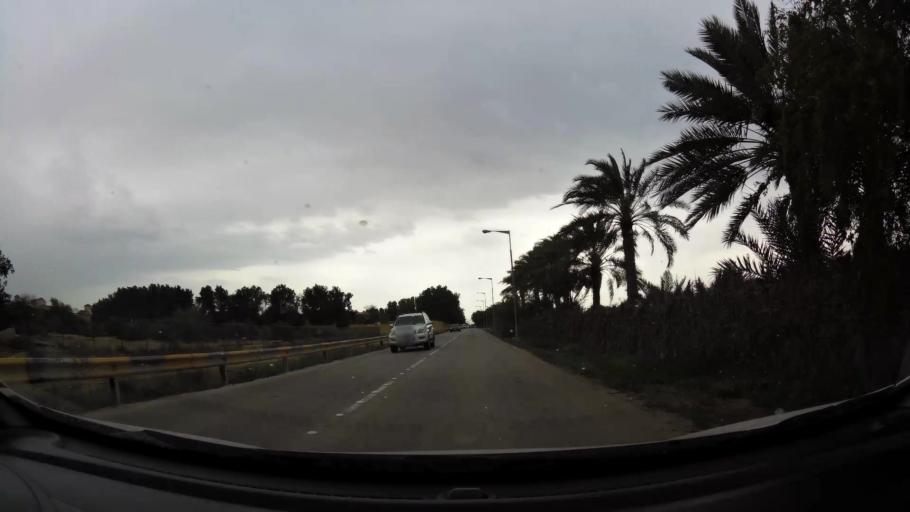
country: BH
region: Central Governorate
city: Madinat Hamad
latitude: 26.1550
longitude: 50.4625
